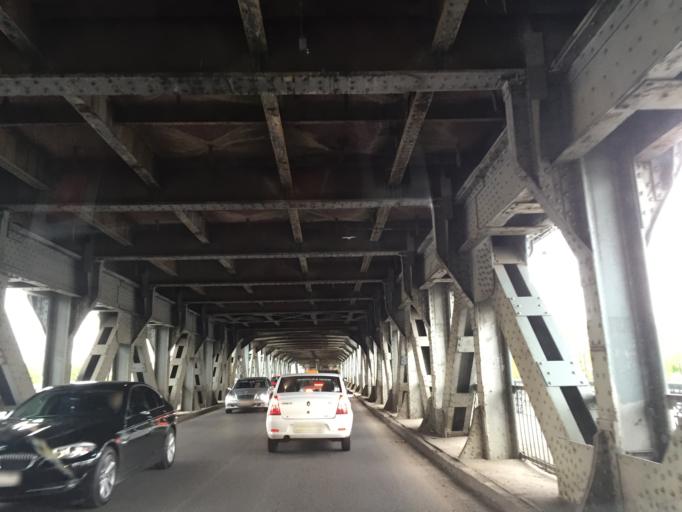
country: RU
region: Kaliningrad
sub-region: Gorod Kaliningrad
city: Kaliningrad
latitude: 54.7061
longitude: 20.4892
